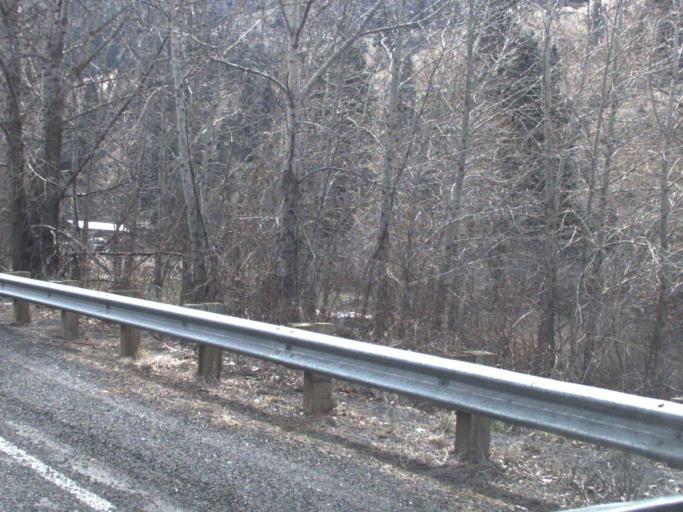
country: US
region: Washington
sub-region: Yakima County
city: Tieton
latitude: 46.7828
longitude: -120.8656
